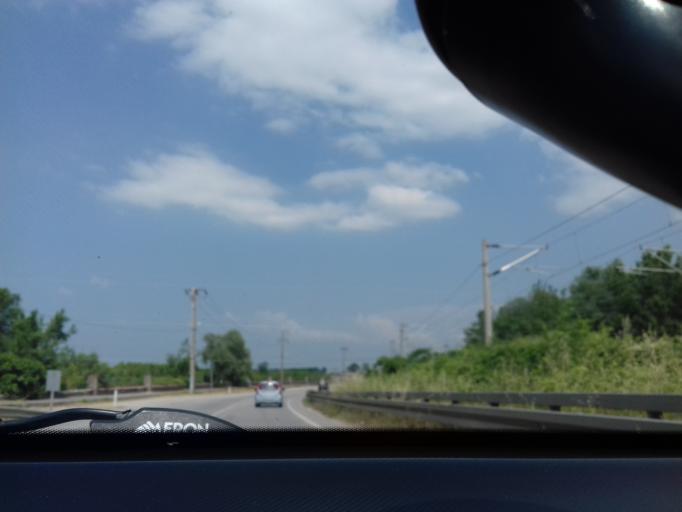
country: TR
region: Sakarya
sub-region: Merkez
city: Sapanca
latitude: 40.7125
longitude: 30.3266
